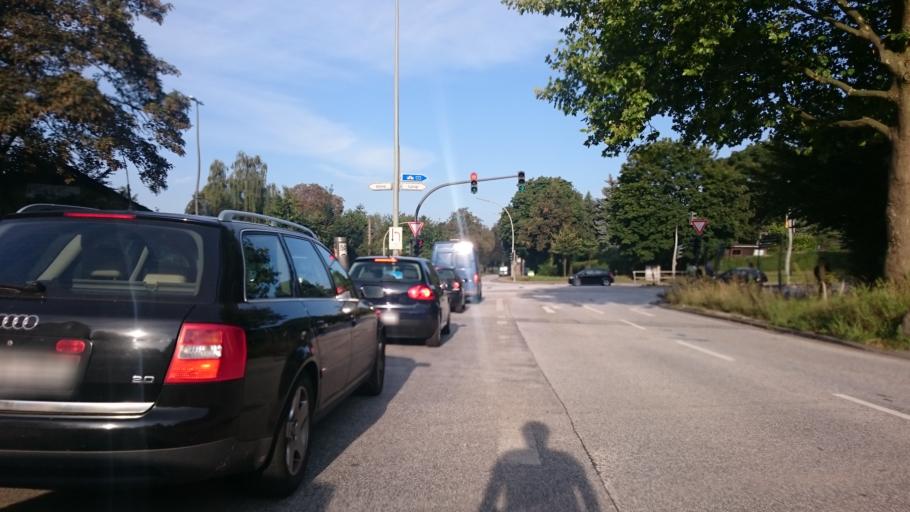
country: DE
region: Hamburg
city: Stellingen
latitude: 53.5708
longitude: 9.9189
